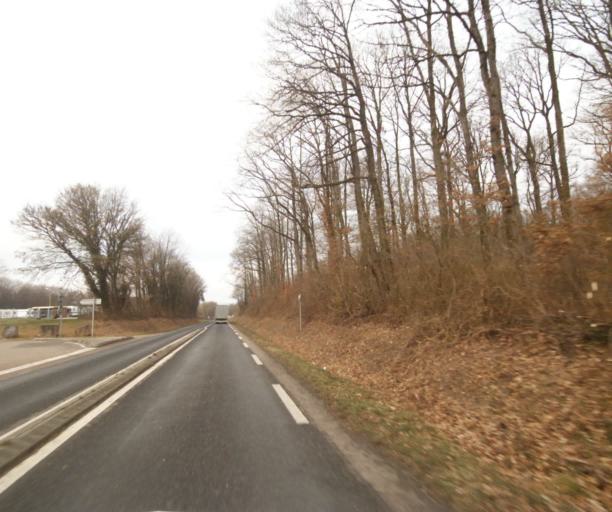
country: FR
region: Champagne-Ardenne
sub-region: Departement de la Haute-Marne
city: Bettancourt-la-Ferree
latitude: 48.6373
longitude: 4.9916
